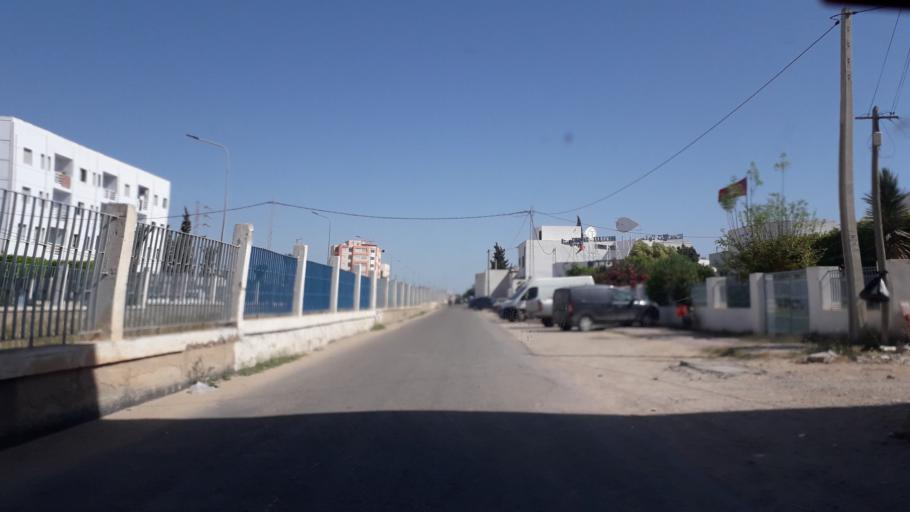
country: TN
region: Safaqis
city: Al Qarmadah
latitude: 34.8054
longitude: 10.7617
